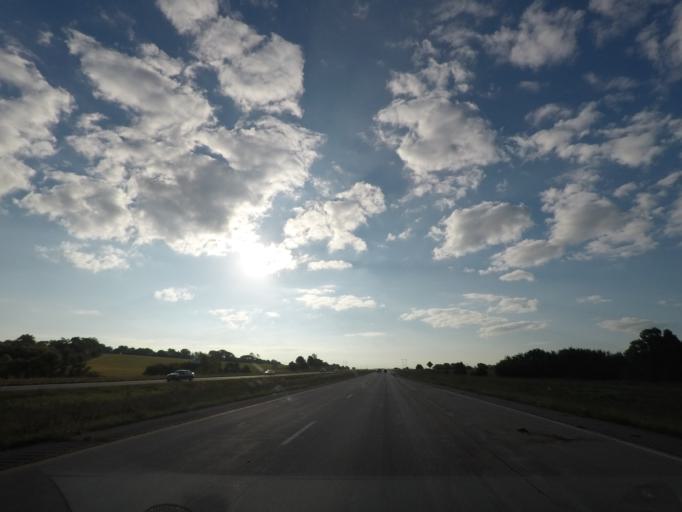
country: US
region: Iowa
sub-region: Warren County
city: Norwalk
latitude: 41.5056
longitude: -93.6413
